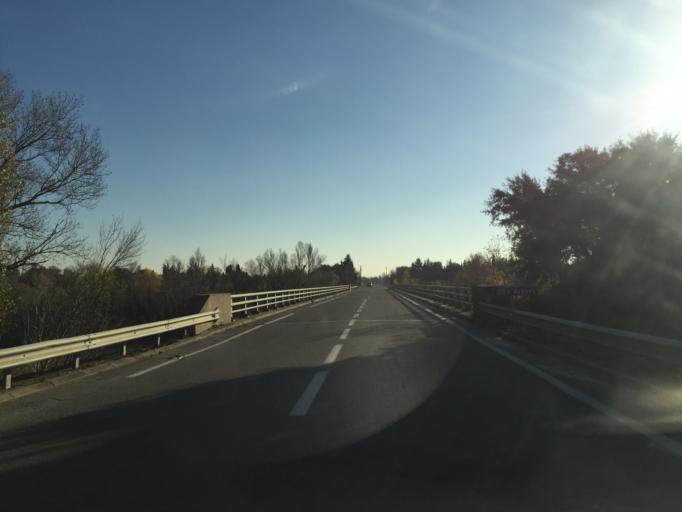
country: FR
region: Provence-Alpes-Cote d'Azur
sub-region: Departement du Vaucluse
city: Serignan-du-Comtat
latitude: 44.1758
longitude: 4.8565
